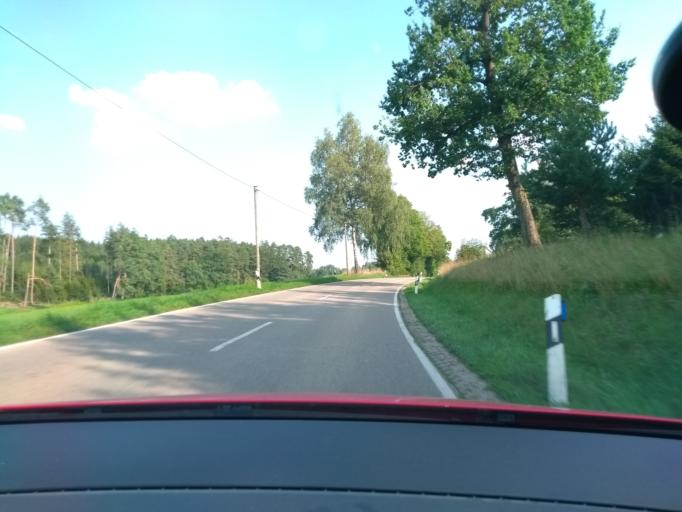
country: DE
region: Bavaria
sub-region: Upper Bavaria
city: Schwabhausen
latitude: 48.3878
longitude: 11.3305
